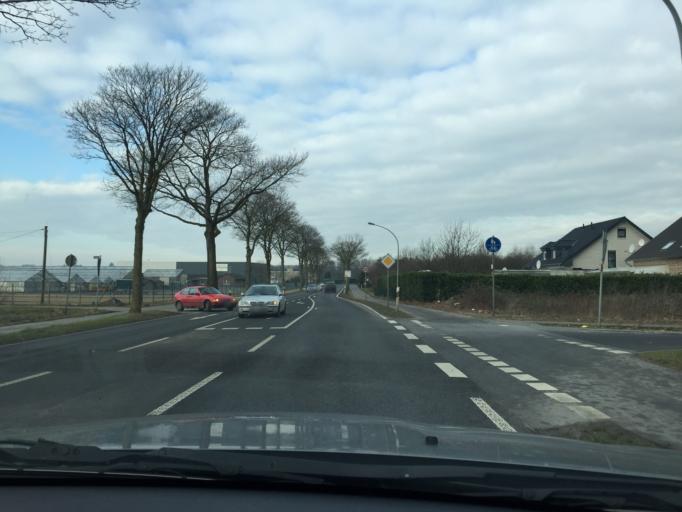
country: DE
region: North Rhine-Westphalia
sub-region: Regierungsbezirk Dusseldorf
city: Kleve
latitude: 51.7692
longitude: 6.1235
